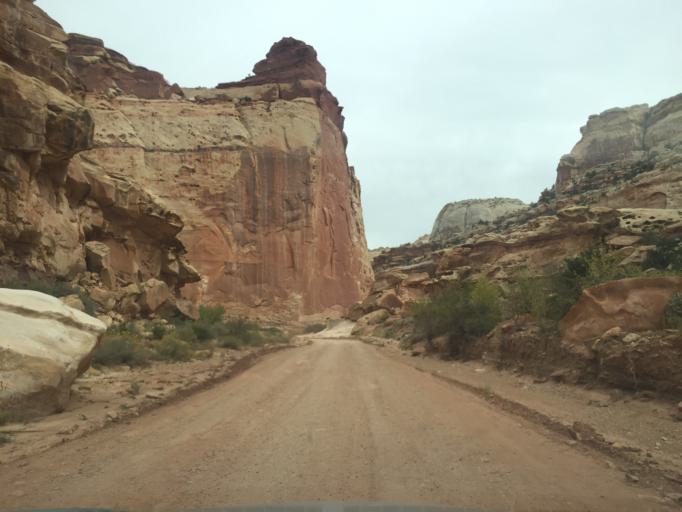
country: US
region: Utah
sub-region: Wayne County
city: Loa
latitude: 38.2608
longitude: -111.2217
